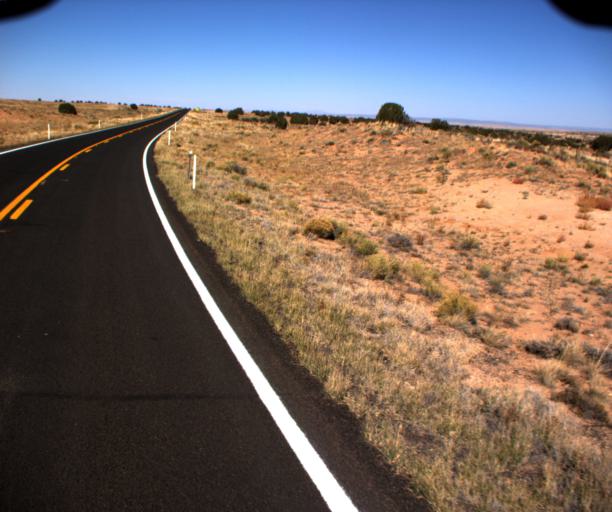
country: US
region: Arizona
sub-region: Coconino County
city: Tuba City
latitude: 35.9089
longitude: -110.8840
